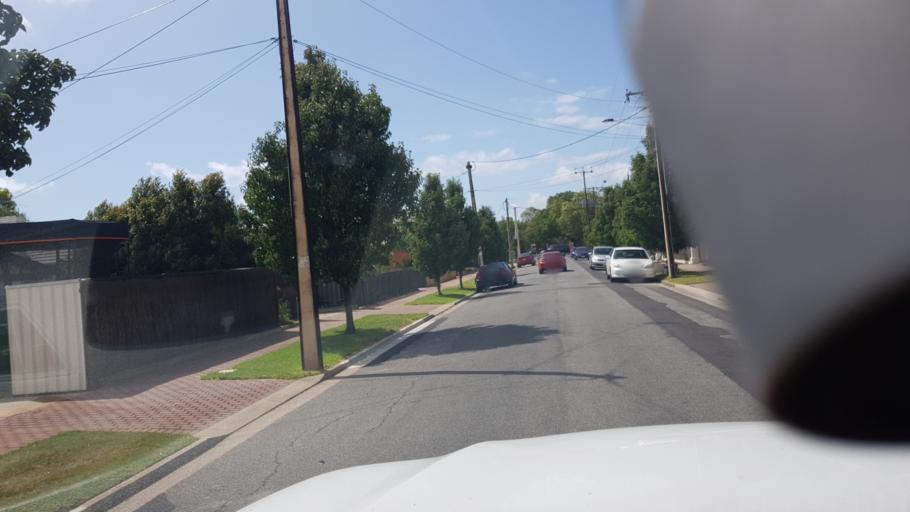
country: AU
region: South Australia
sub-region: Holdfast Bay
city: Glenelg East
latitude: -34.9771
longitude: 138.5313
